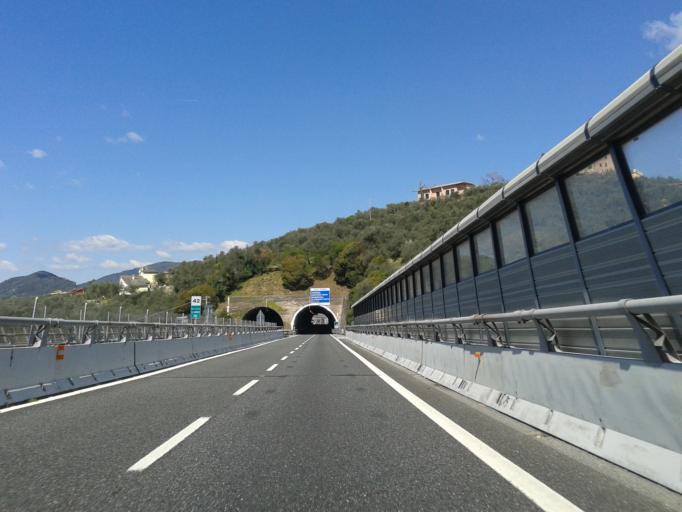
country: IT
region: Liguria
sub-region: Provincia di Genova
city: Lavagna
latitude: 44.3121
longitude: 9.3591
